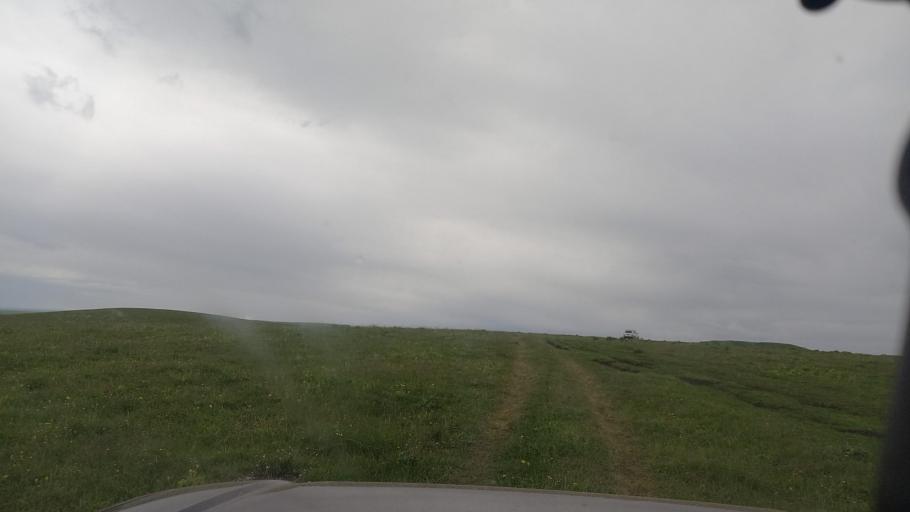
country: RU
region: Karachayevo-Cherkesiya
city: Pregradnaya
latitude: 43.9836
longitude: 41.2918
